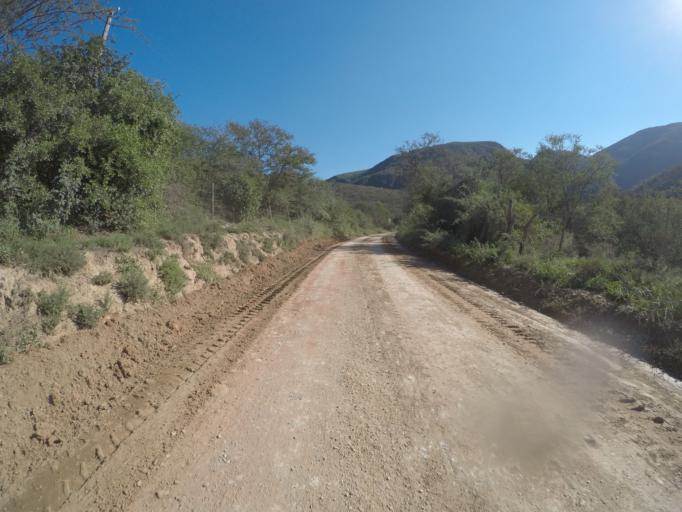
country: ZA
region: Eastern Cape
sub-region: Cacadu District Municipality
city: Kareedouw
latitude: -33.6635
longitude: 24.5411
